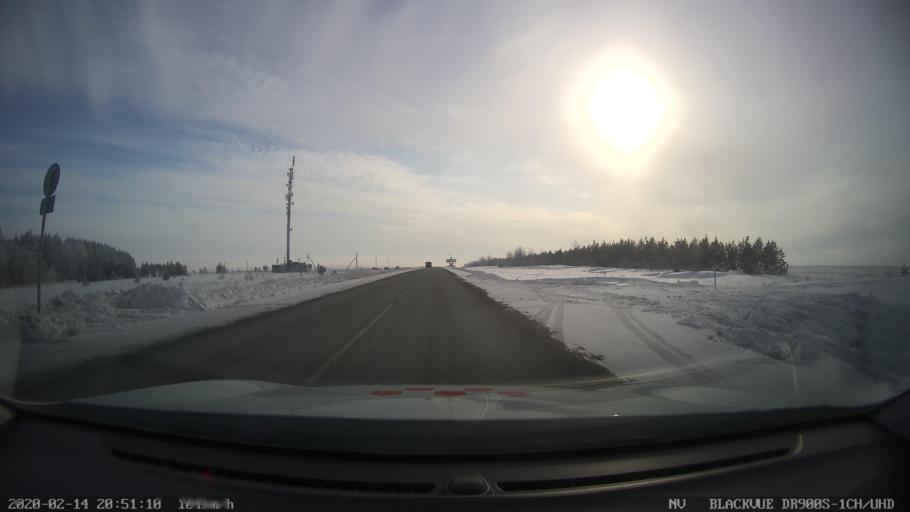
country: RU
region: Tatarstan
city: Kuybyshevskiy Zaton
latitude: 55.2162
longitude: 49.2347
